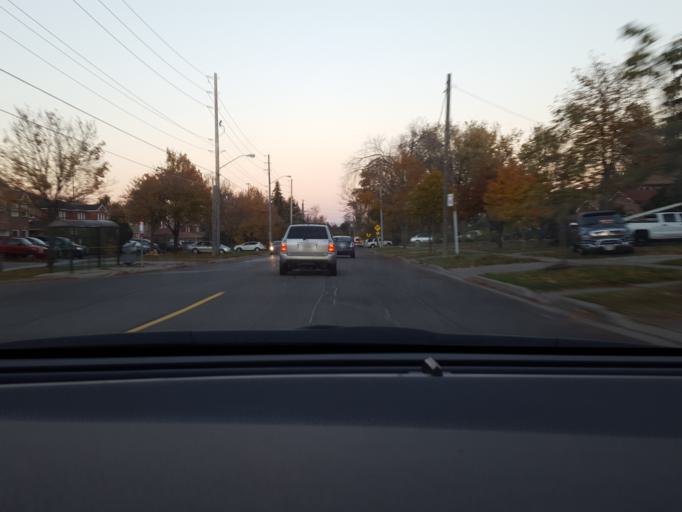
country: CA
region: Ontario
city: Scarborough
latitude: 43.7938
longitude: -79.1580
